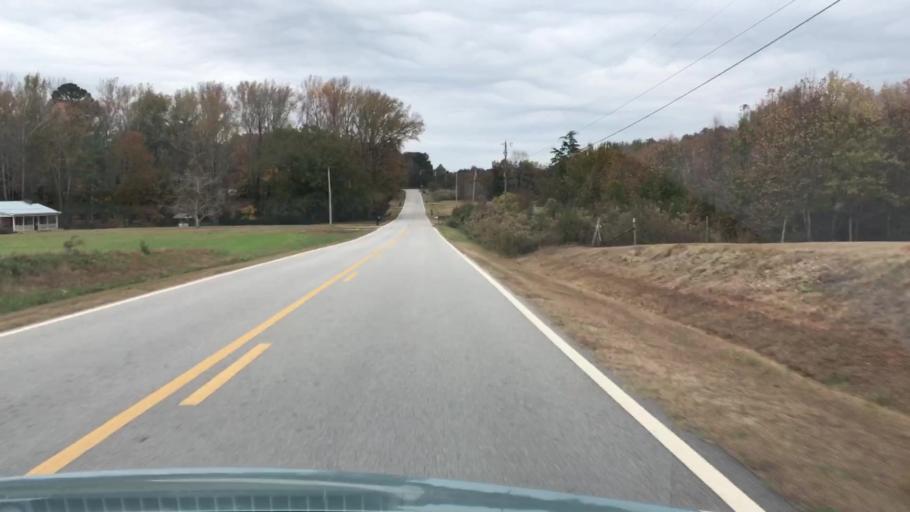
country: US
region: Georgia
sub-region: Henry County
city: McDonough
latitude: 33.5119
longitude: -84.1235
